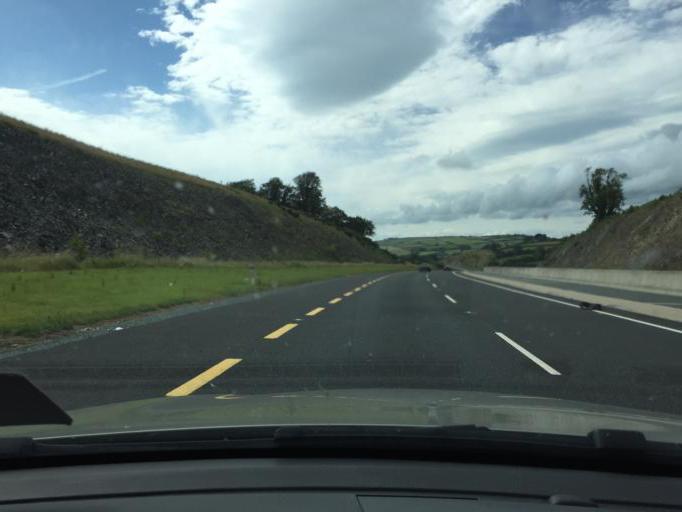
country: IE
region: Leinster
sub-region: Kilkenny
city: Mooncoin
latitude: 52.2356
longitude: -7.2319
